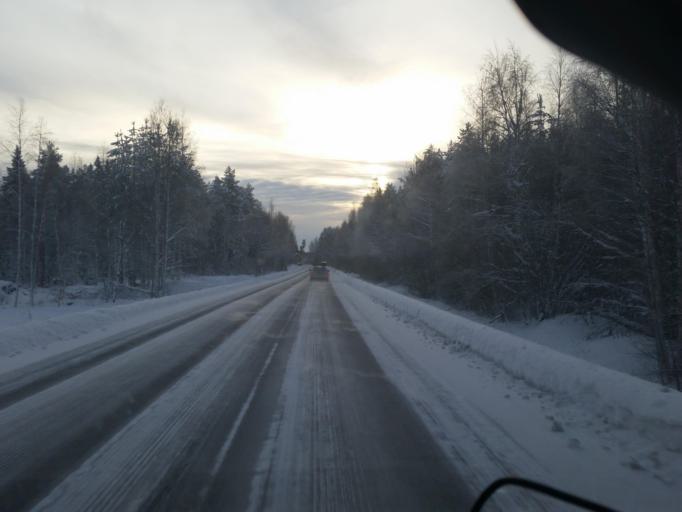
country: SE
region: Norrbotten
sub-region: Pitea Kommun
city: Norrfjarden
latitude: 65.4506
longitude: 21.4568
